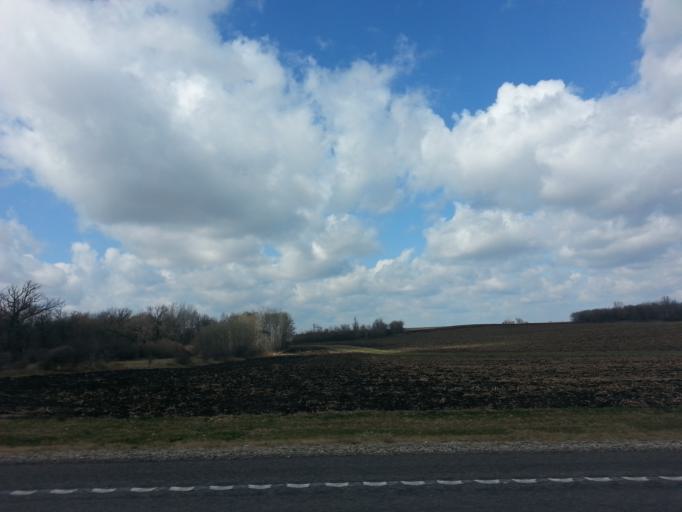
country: US
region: Minnesota
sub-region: Dodge County
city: Mantorville
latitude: 44.0799
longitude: -92.7446
